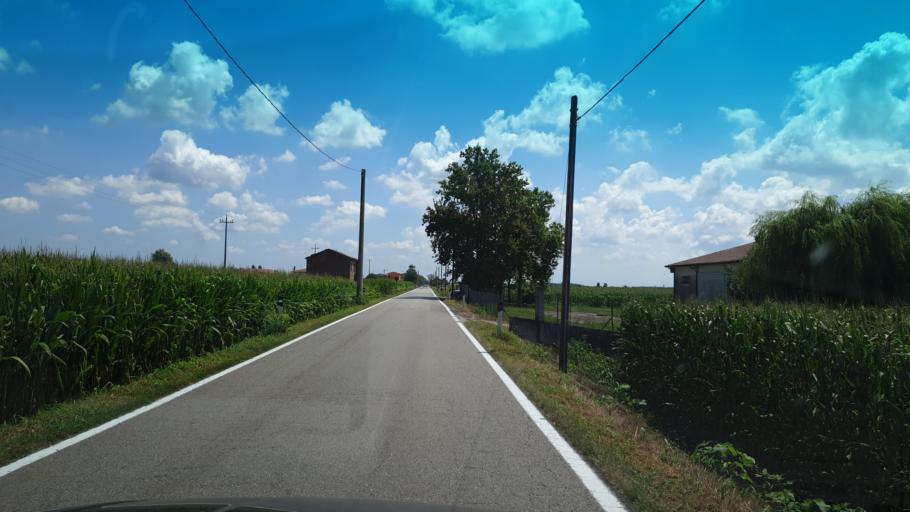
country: IT
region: Veneto
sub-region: Provincia di Padova
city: Boara Pisani
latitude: 45.1485
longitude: 11.8056
